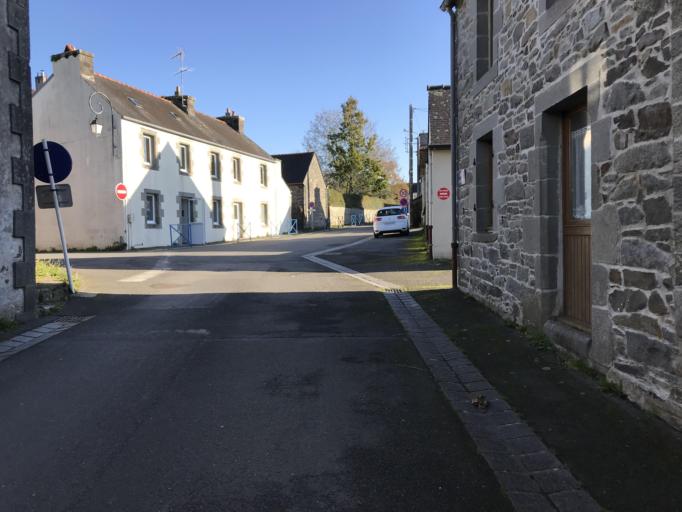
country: FR
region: Brittany
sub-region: Departement du Finistere
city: Hopital-Camfrout
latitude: 48.3278
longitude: -4.2419
